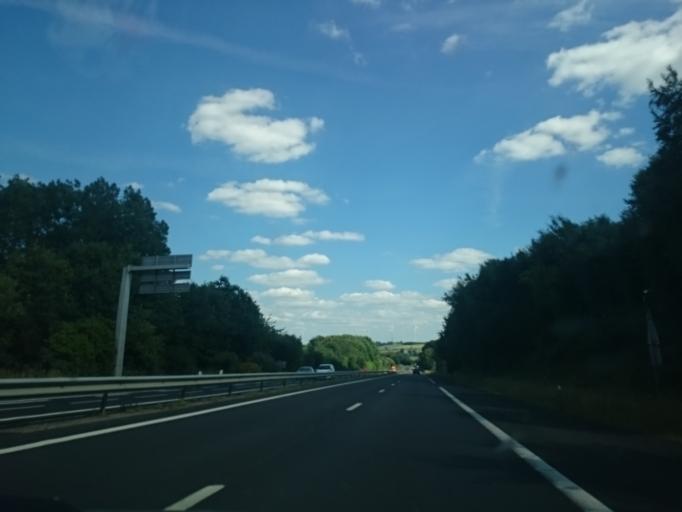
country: FR
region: Brittany
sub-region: Departement des Cotes-d'Armor
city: Saint-Barnabe
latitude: 48.1742
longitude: -2.6554
